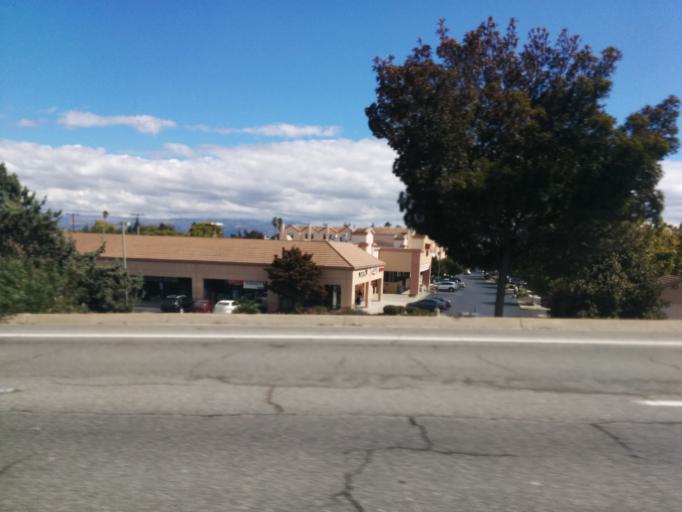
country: US
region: California
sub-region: Santa Clara County
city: Cupertino
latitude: 37.3237
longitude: -121.9959
